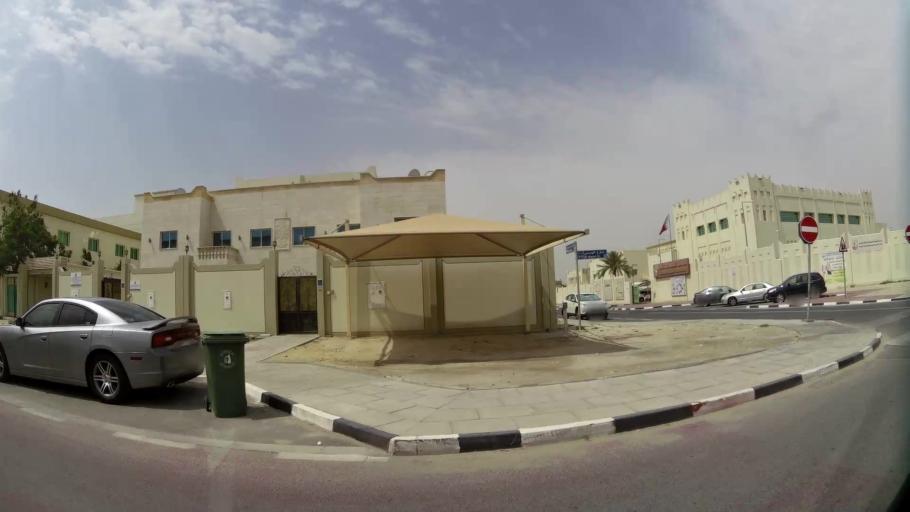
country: QA
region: Baladiyat ad Dawhah
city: Doha
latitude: 25.3085
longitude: 51.4768
